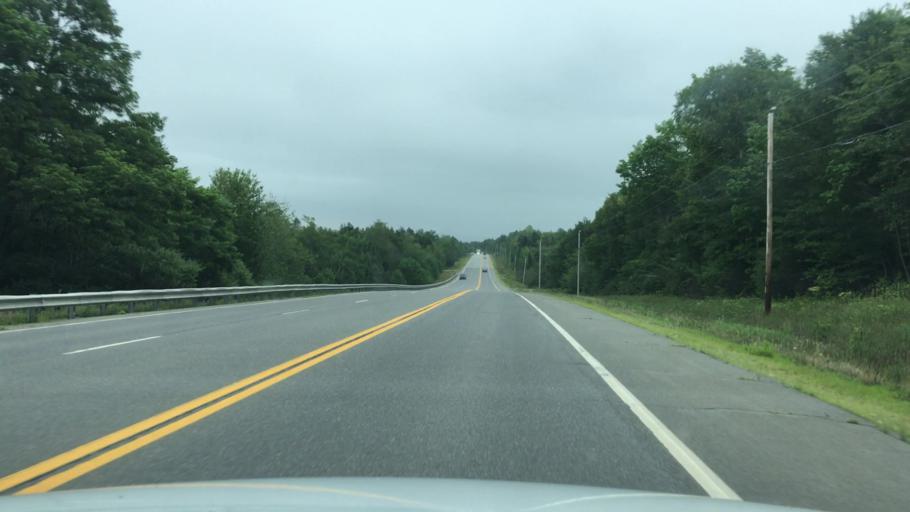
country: US
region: Maine
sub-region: Hancock County
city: Franklin
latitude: 44.8269
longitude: -68.1193
